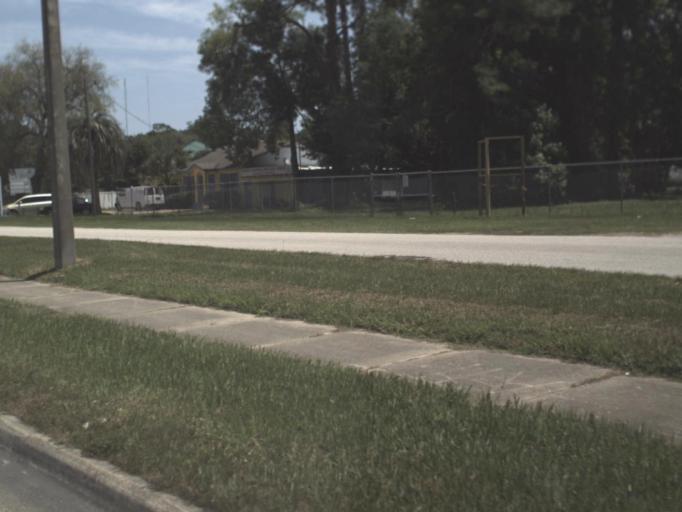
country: US
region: Florida
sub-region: Duval County
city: Jacksonville
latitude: 30.2895
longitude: -81.5871
